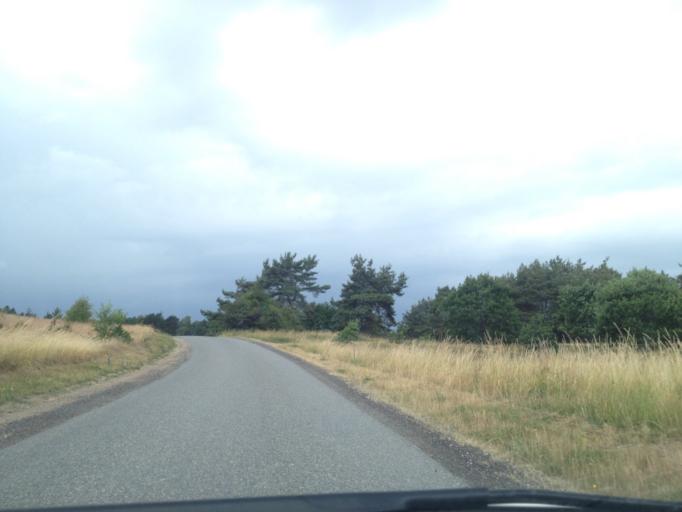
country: DK
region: Central Jutland
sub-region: Syddjurs Kommune
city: Ebeltoft
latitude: 56.1639
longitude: 10.6839
